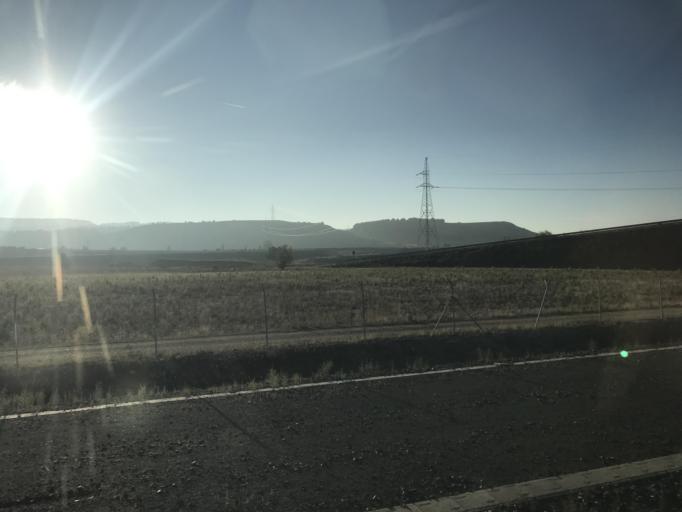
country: ES
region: Castille and Leon
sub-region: Provincia de Valladolid
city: Santovenia de Pisuerga
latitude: 41.7012
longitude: -4.6757
